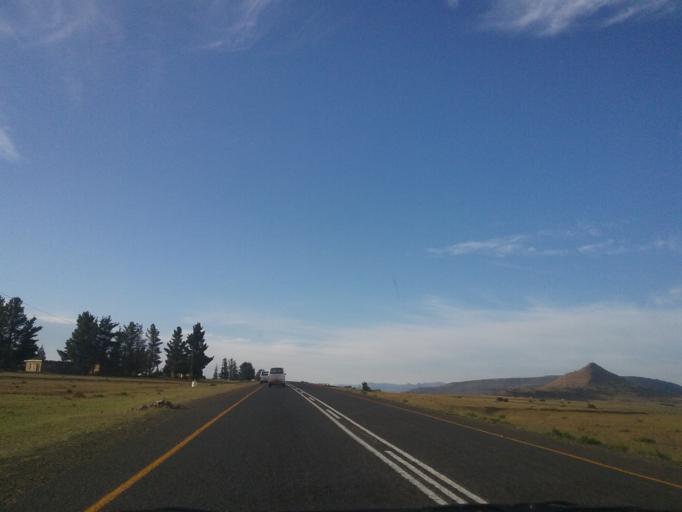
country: LS
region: Mohale's Hoek District
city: Mohale's Hoek
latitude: -30.2094
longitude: 27.4316
